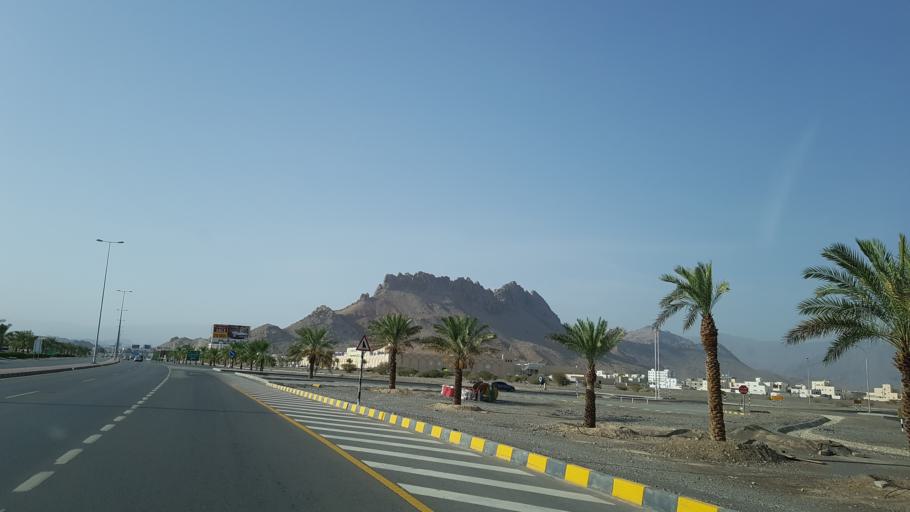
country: OM
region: Muhafazat ad Dakhiliyah
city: Nizwa
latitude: 22.8662
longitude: 57.5377
